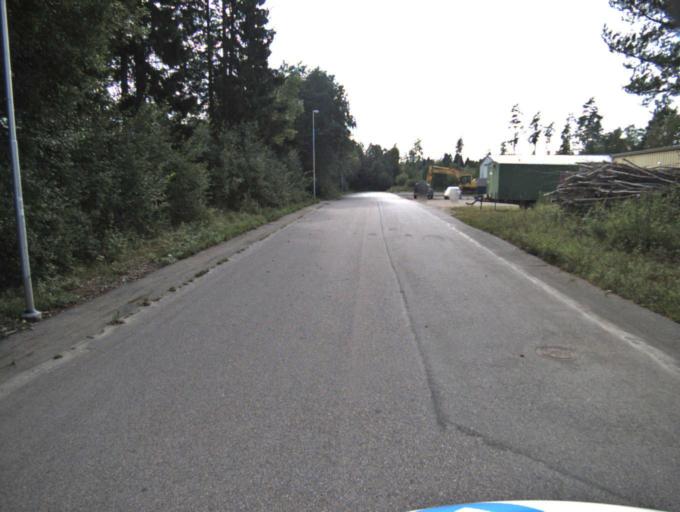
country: SE
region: Vaestra Goetaland
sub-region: Ulricehamns Kommun
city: Ulricehamn
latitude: 57.8340
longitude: 13.2726
